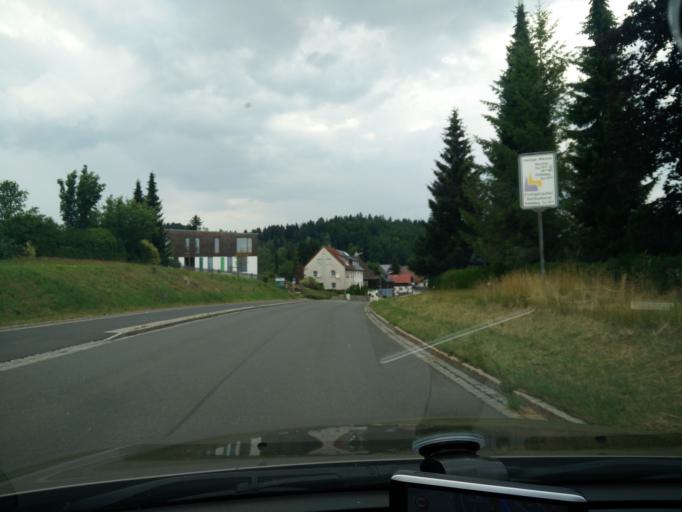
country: DE
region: Bavaria
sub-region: Upper Franconia
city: Fichtelberg
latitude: 49.9963
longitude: 11.8504
